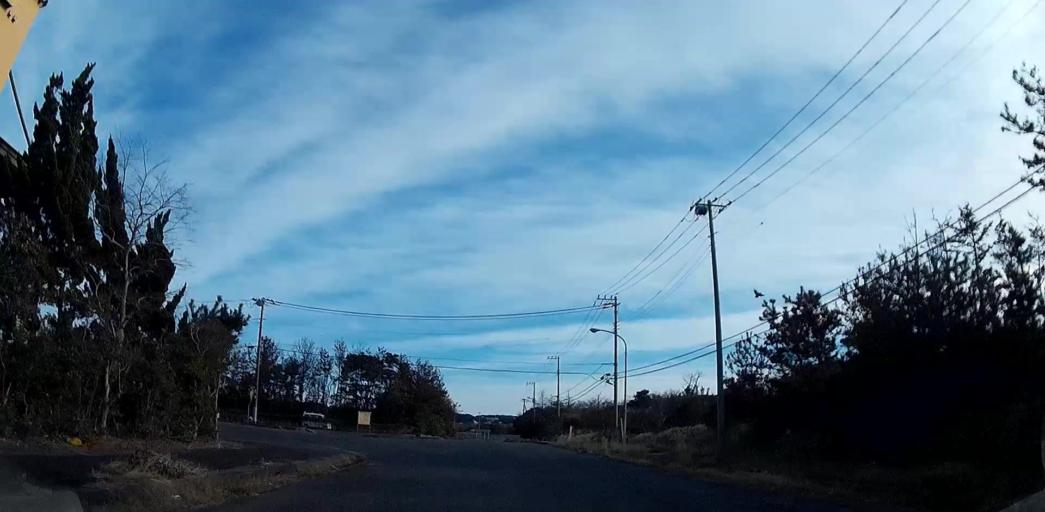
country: JP
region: Chiba
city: Hasaki
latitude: 35.7443
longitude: 140.8407
